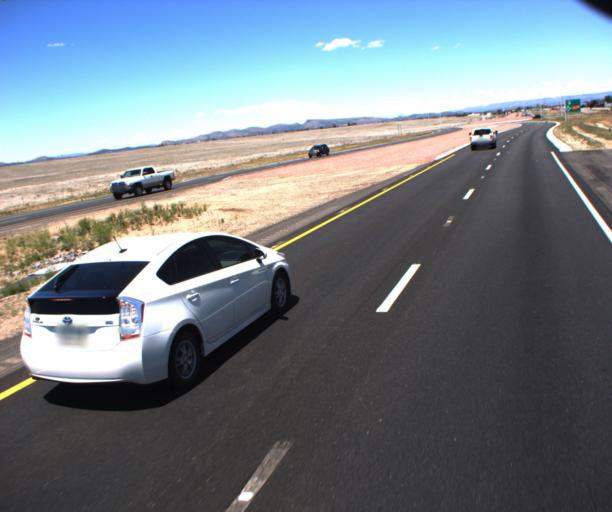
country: US
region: Arizona
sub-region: Yavapai County
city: Chino Valley
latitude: 34.7023
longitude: -112.4495
